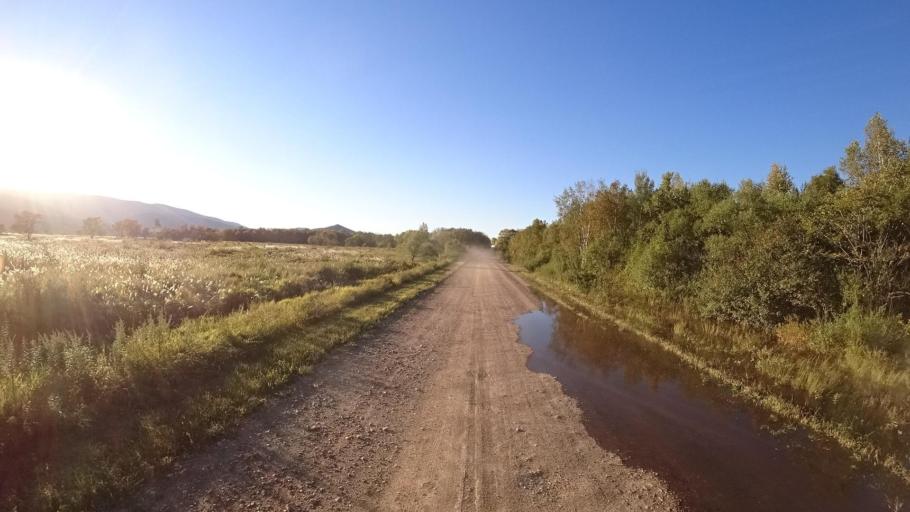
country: RU
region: Primorskiy
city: Kirovskiy
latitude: 44.8164
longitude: 133.6108
